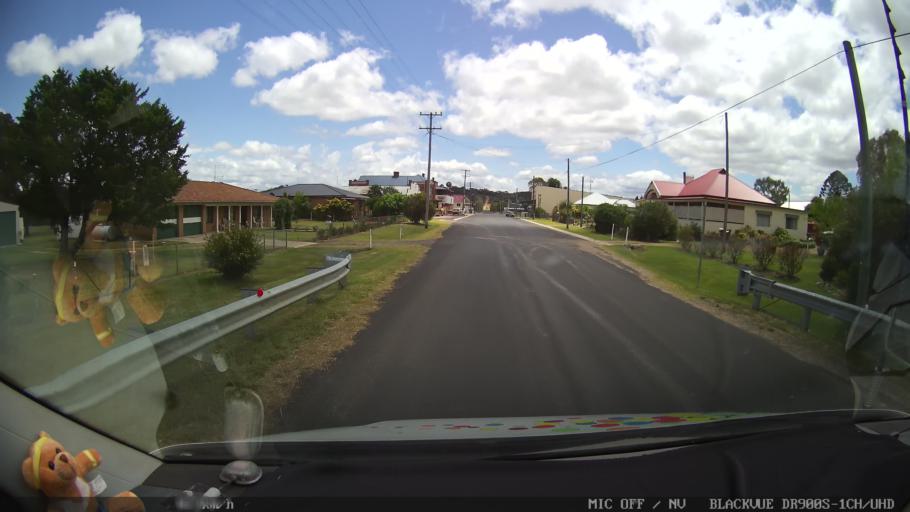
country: AU
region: New South Wales
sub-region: Glen Innes Severn
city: Glen Innes
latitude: -29.4462
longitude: 151.5979
